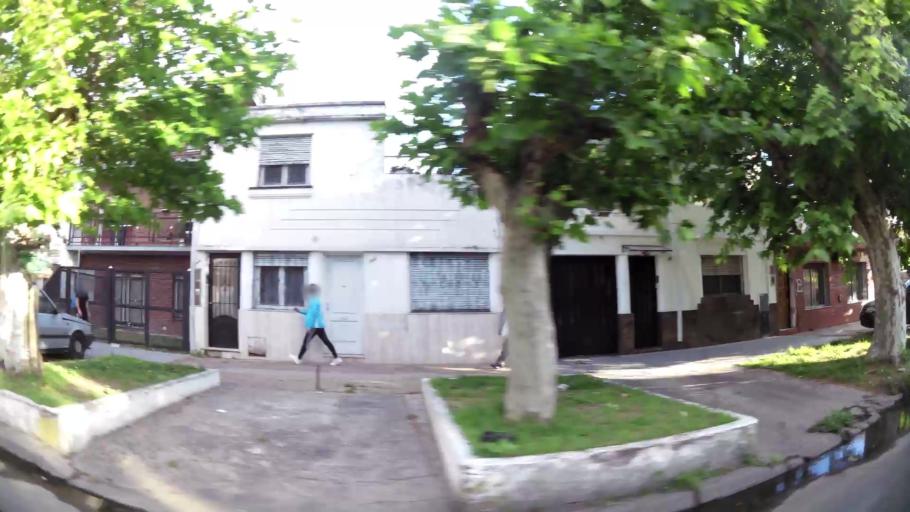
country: AR
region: Buenos Aires
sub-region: Partido de Avellaneda
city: Avellaneda
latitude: -34.6807
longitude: -58.3481
